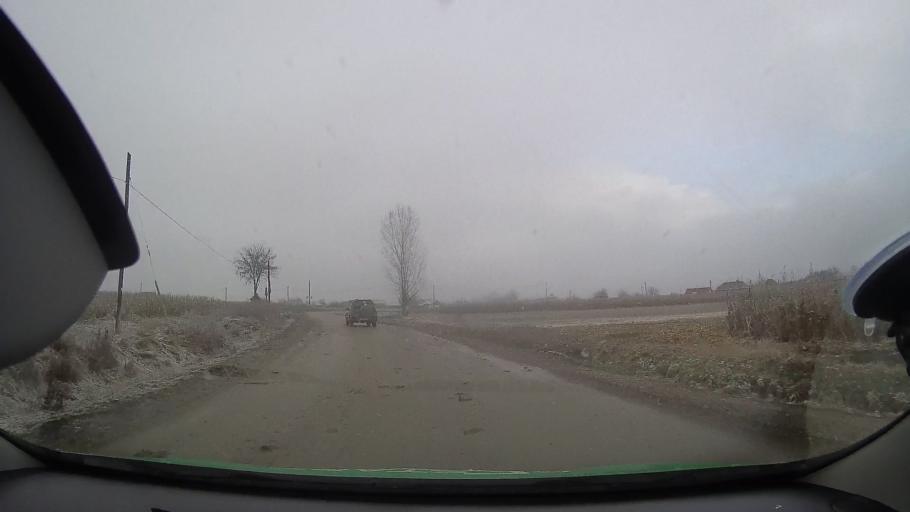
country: RO
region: Alba
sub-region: Comuna Noslac
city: Noslac
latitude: 46.3972
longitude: 23.9173
